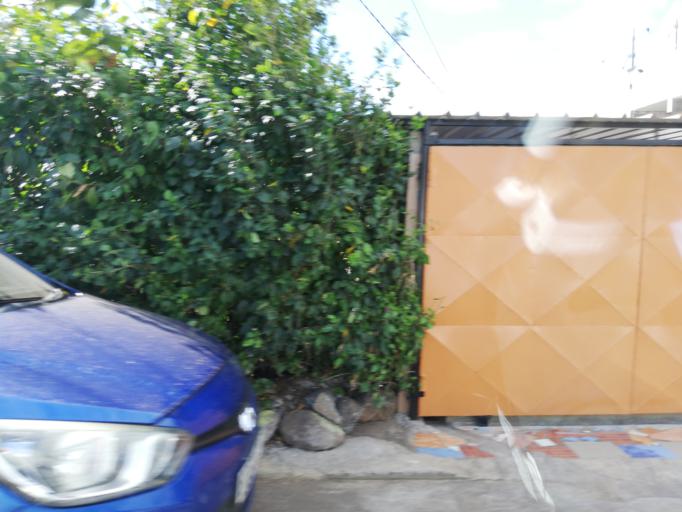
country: MU
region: Black River
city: Petite Riviere
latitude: -20.2227
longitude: 57.4579
